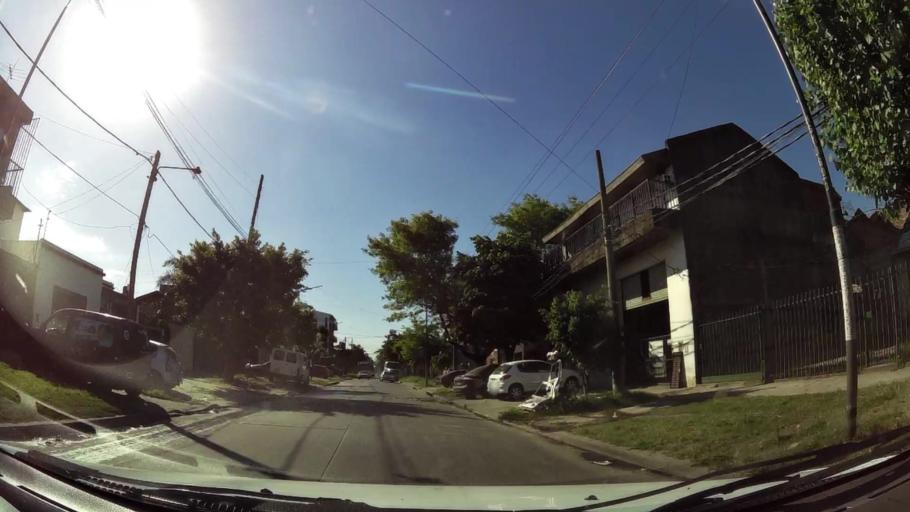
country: AR
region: Buenos Aires
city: Hurlingham
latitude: -34.5609
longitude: -58.6007
